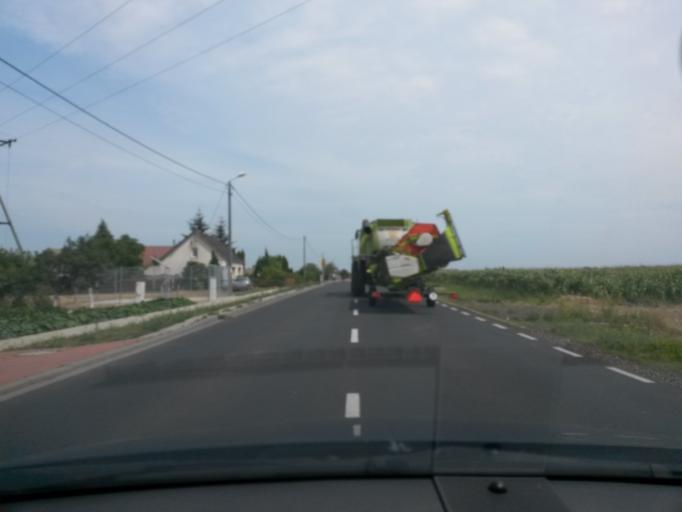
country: PL
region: Greater Poland Voivodeship
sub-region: Powiat sremski
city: Dolsk
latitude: 51.9467
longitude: 17.0480
